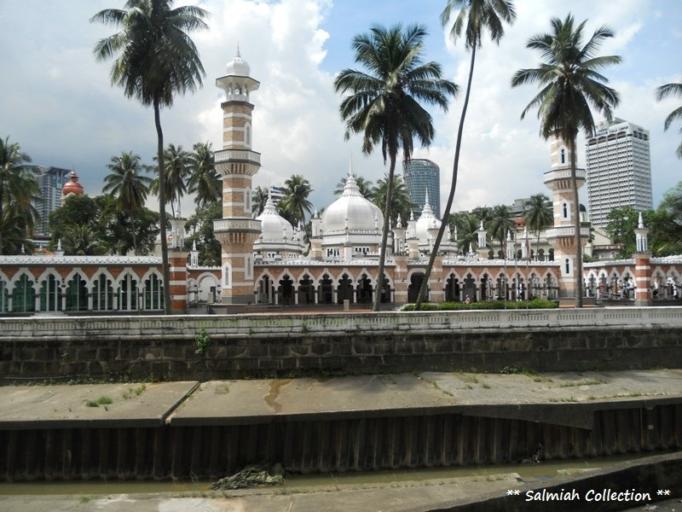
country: MY
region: Kuala Lumpur
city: Kuala Lumpur
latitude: 3.1489
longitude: 101.6956
